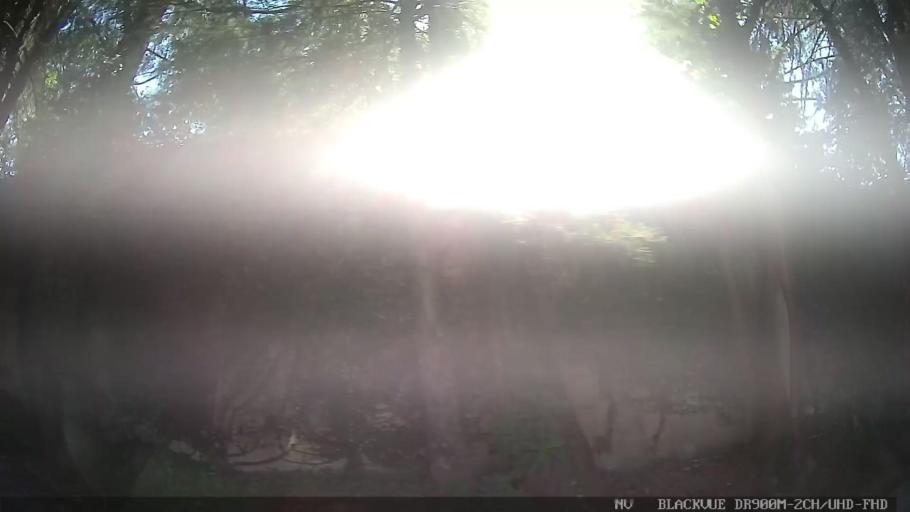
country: BR
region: Sao Paulo
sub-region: Atibaia
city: Atibaia
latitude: -23.1071
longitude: -46.5953
